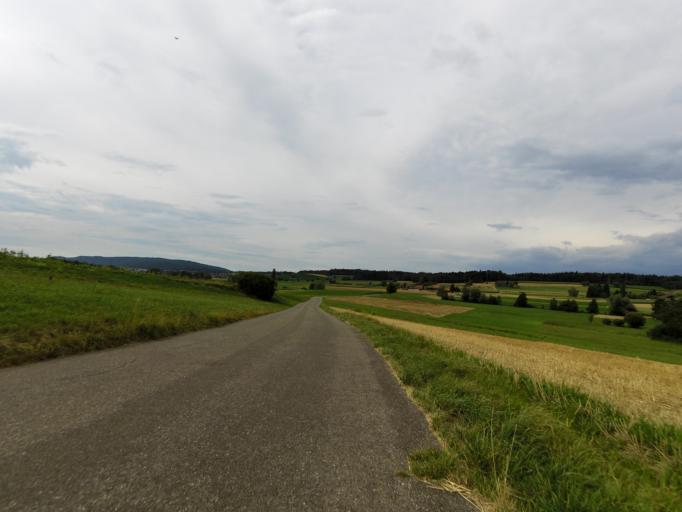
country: CH
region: Zurich
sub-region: Bezirk Zuerich
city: Zuerich (Kreis 11) / Affoltern
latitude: 47.4313
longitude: 8.5027
